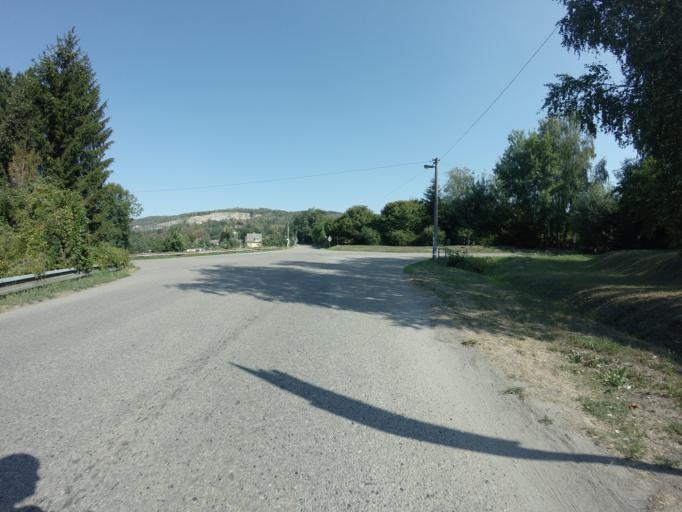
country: CZ
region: Central Bohemia
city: Tynec nad Sazavou
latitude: 49.8505
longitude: 14.5522
